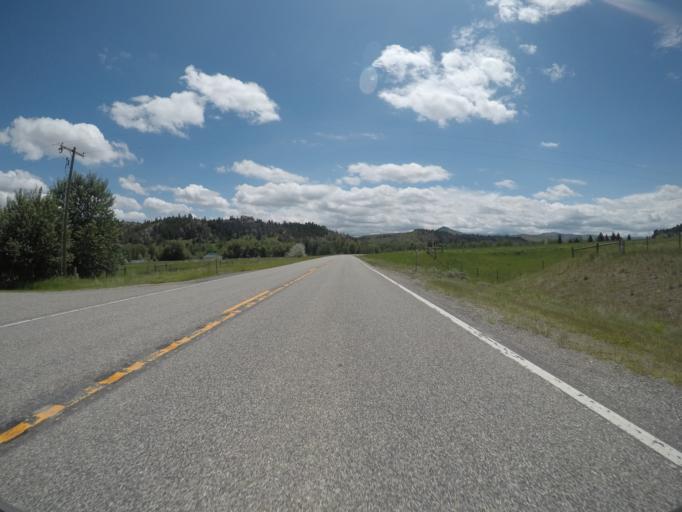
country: US
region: Montana
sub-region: Sweet Grass County
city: Big Timber
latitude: 45.7269
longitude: -109.9978
